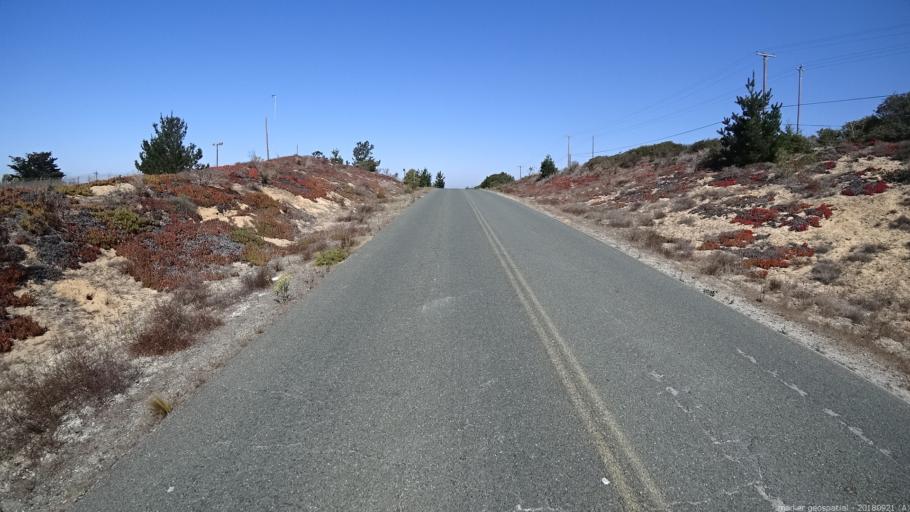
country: US
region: California
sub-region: Monterey County
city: Marina
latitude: 36.6444
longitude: -121.7873
